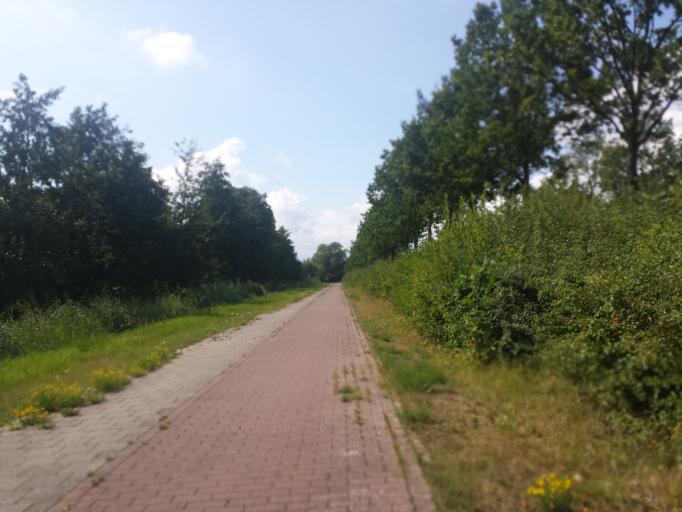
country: DE
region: Lower Saxony
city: Stuhr
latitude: 53.0874
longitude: 8.7230
